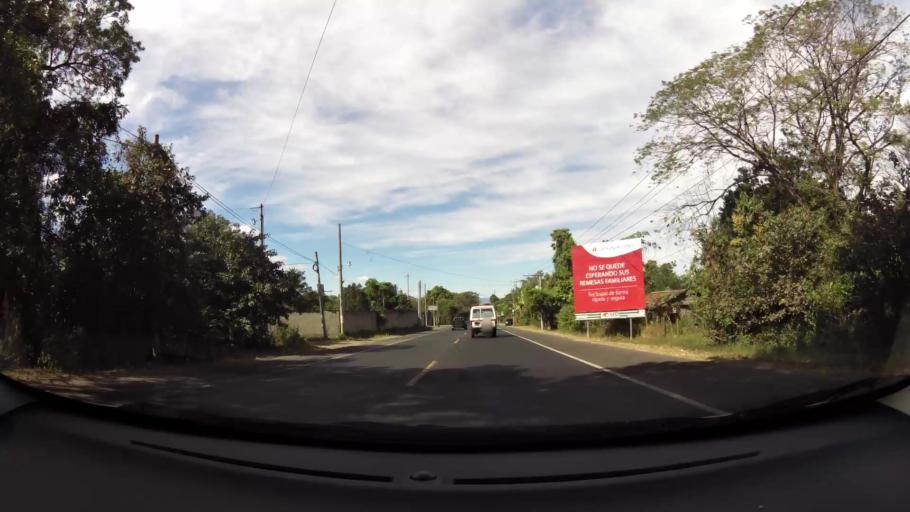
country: SV
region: San Salvador
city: Aguilares
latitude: 13.9338
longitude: -89.1871
